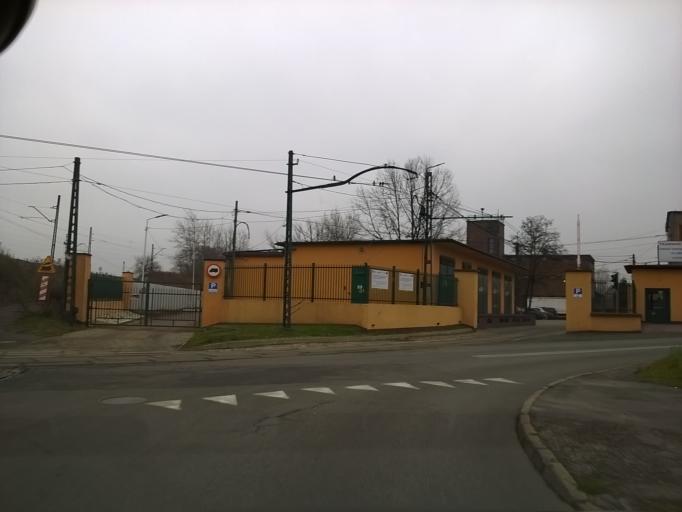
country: PL
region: Silesian Voivodeship
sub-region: Chorzow
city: Chorzow
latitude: 50.2738
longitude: 18.9552
